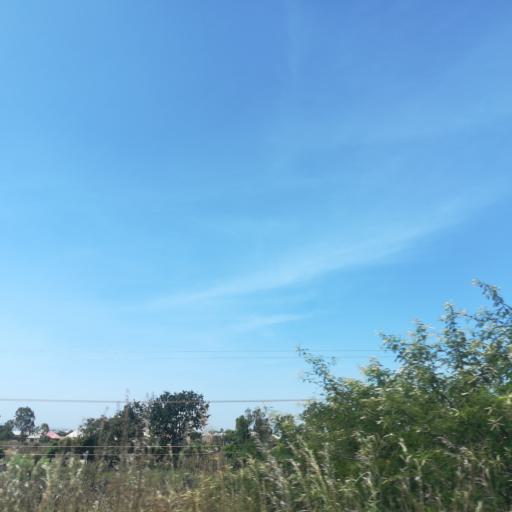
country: NG
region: Plateau
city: Bukuru
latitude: 9.7842
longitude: 8.8828
